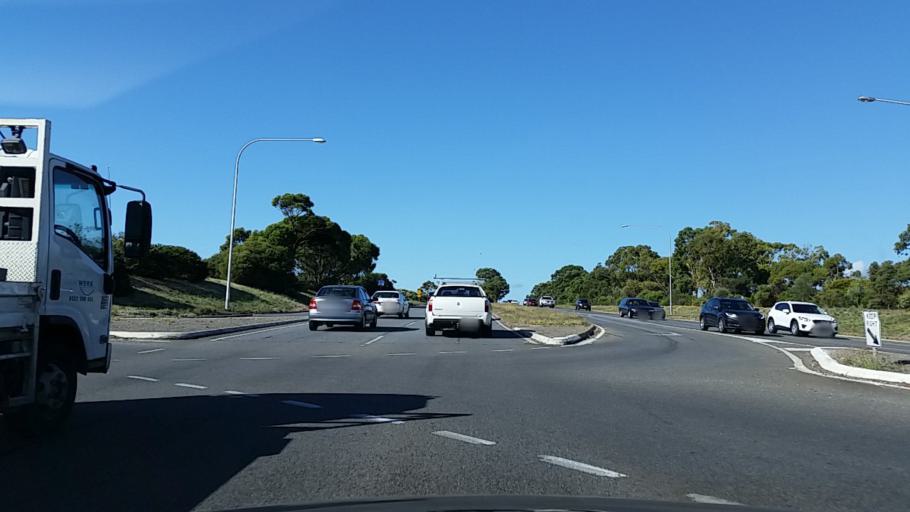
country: AU
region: South Australia
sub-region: Marion
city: Happy Valley
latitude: -35.0699
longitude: 138.5276
